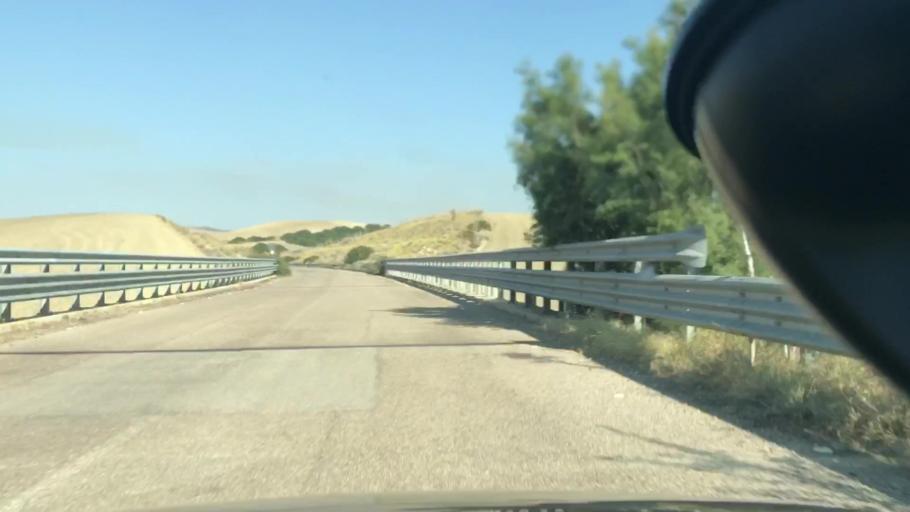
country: IT
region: Basilicate
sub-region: Provincia di Matera
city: La Martella
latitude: 40.6887
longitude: 16.4475
